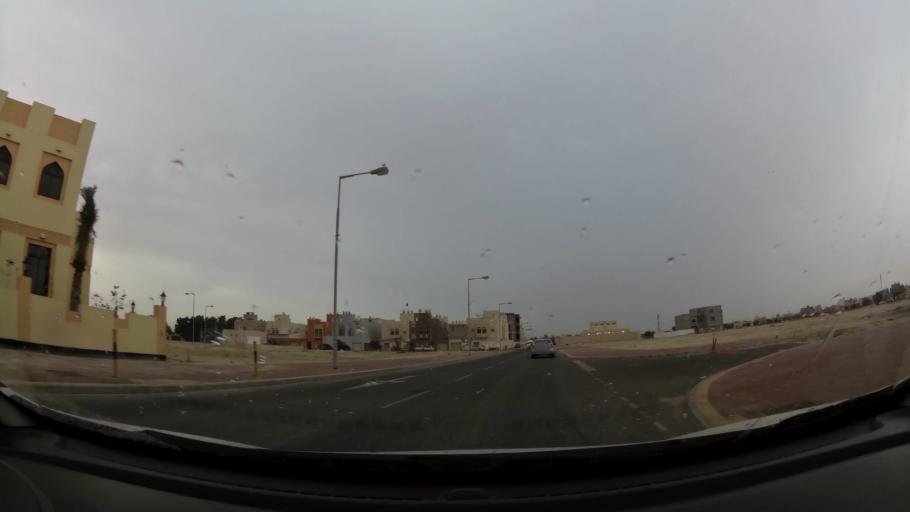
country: BH
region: Central Governorate
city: Madinat Hamad
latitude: 26.1155
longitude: 50.4886
